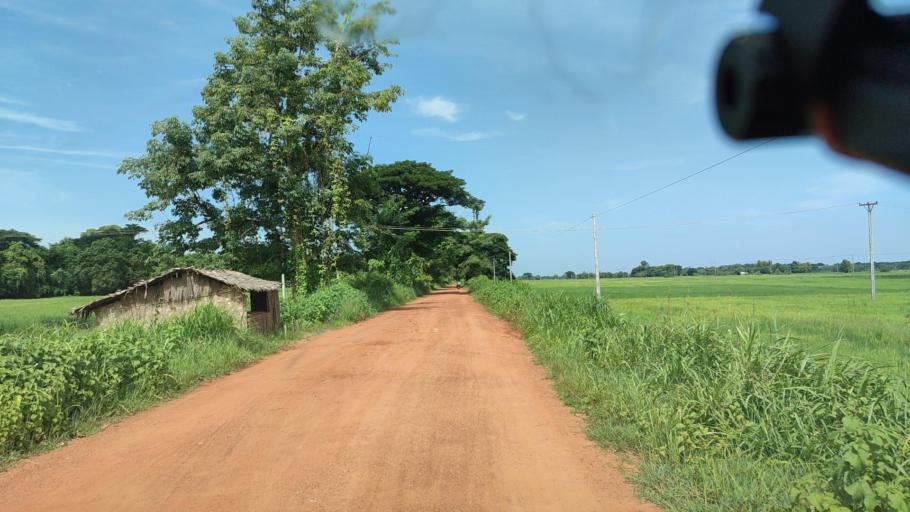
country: MM
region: Ayeyarwady
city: Hinthada
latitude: 17.6926
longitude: 95.5235
